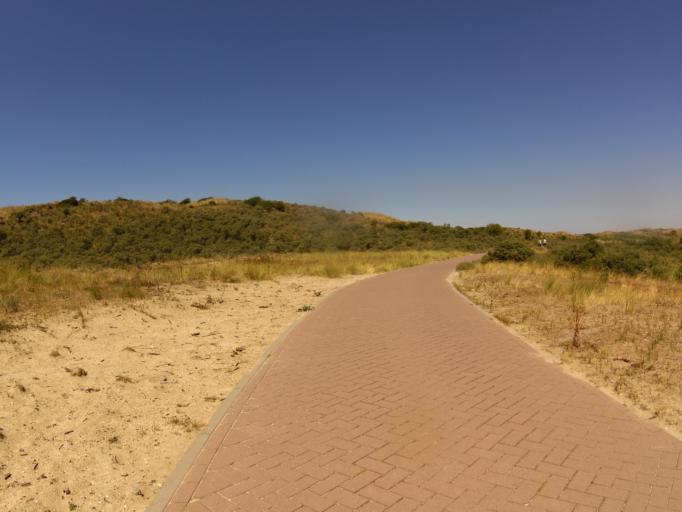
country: NL
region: North Holland
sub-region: Gemeente Bloemendaal
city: Bloemendaal
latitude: 52.4214
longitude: 4.5691
